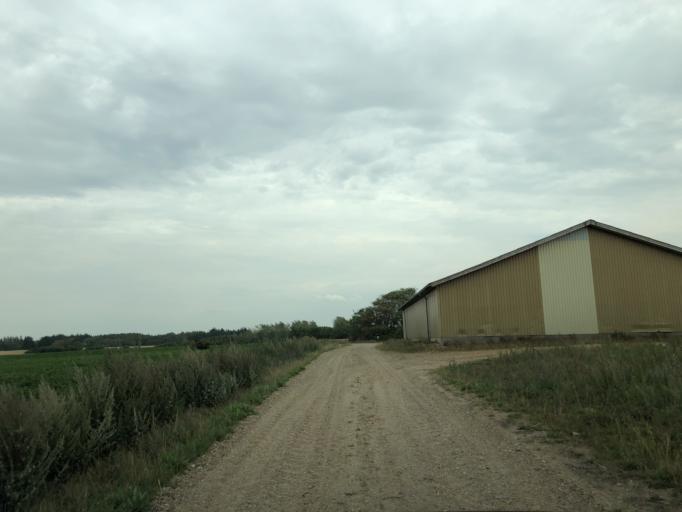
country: DK
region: Central Jutland
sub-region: Holstebro Kommune
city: Ulfborg
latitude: 56.2402
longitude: 8.3705
